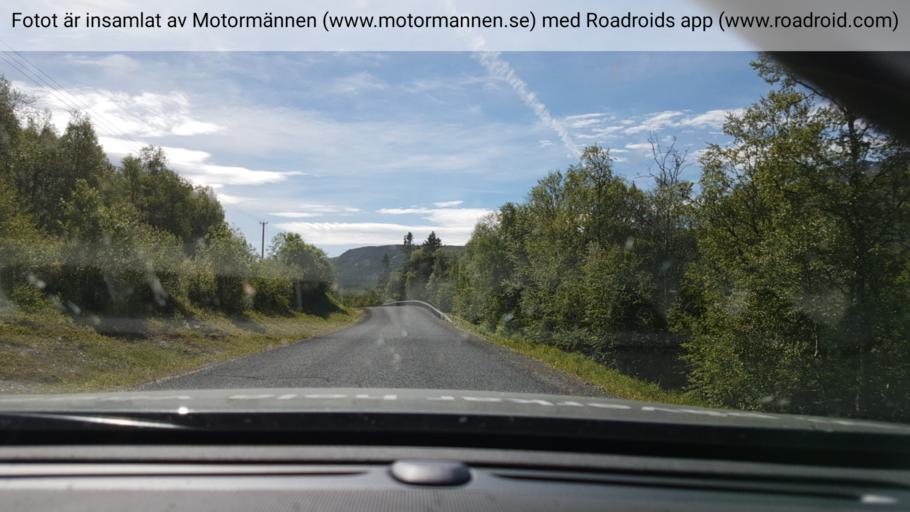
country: SE
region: Vaesterbotten
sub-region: Vilhelmina Kommun
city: Sjoberg
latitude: 65.2918
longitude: 15.2932
